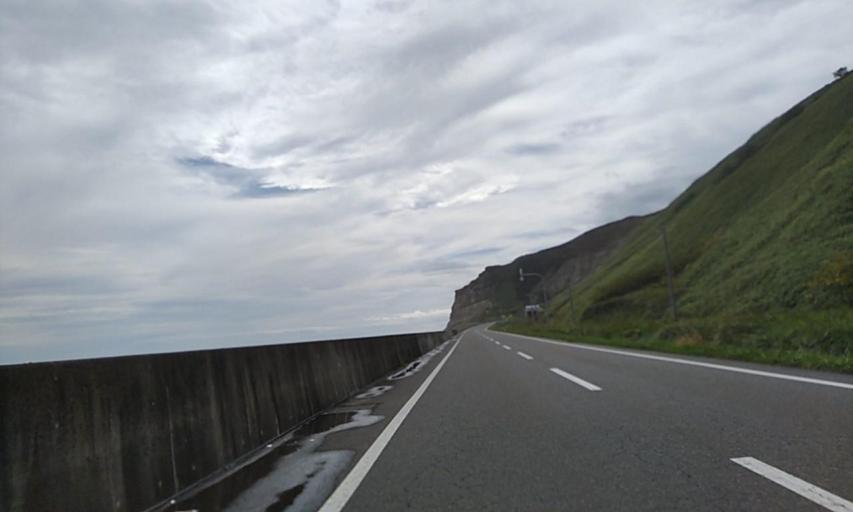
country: JP
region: Hokkaido
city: Obihiro
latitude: 42.7676
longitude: 143.7681
